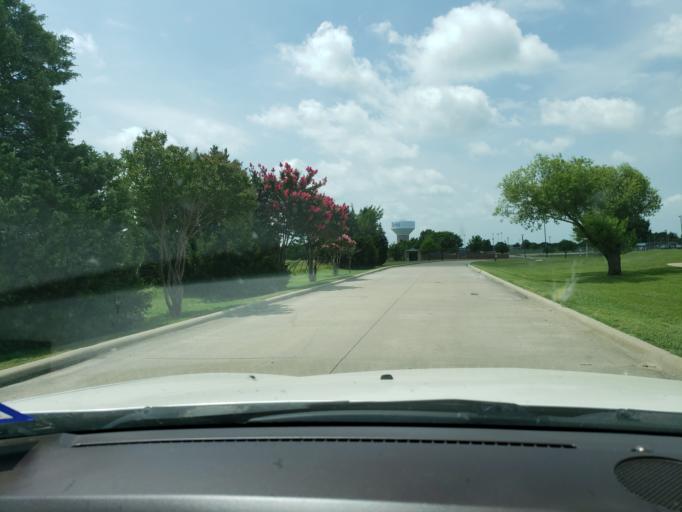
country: US
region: Texas
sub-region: Dallas County
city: Rowlett
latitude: 32.9028
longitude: -96.5589
